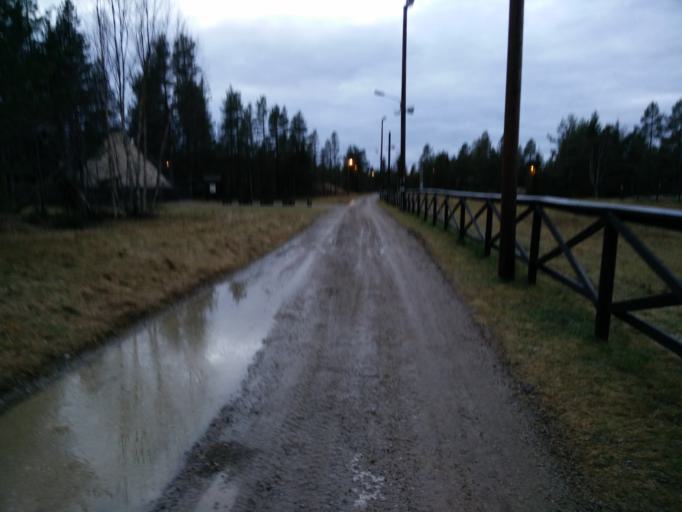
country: SE
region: Vaesternorrland
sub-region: Sundsvalls Kommun
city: Sundsvall
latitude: 62.3662
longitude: 17.3072
